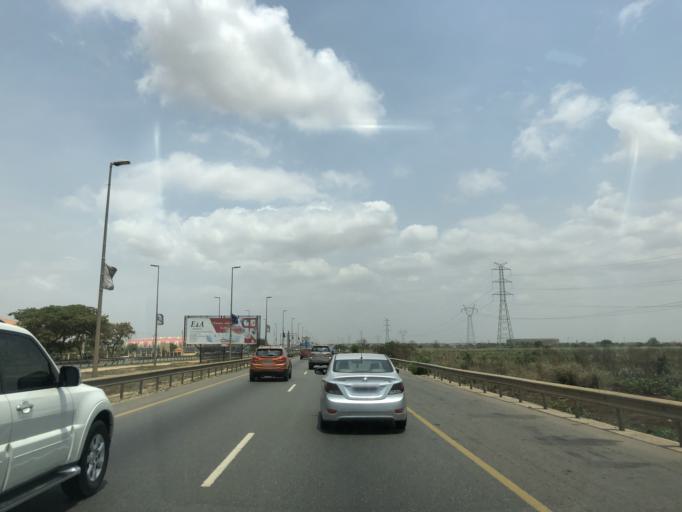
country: AO
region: Luanda
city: Luanda
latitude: -8.9737
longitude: 13.2695
